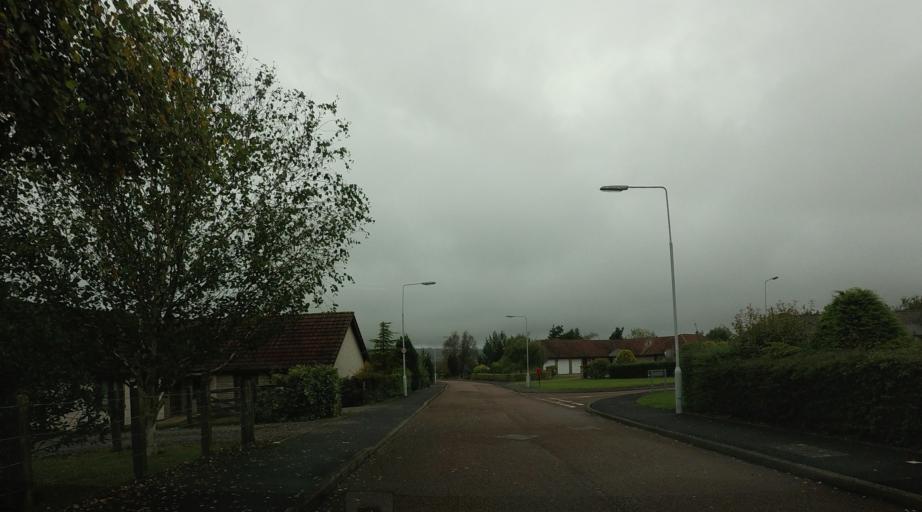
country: GB
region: Scotland
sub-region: Fife
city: Balmullo
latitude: 56.4090
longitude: -2.9103
